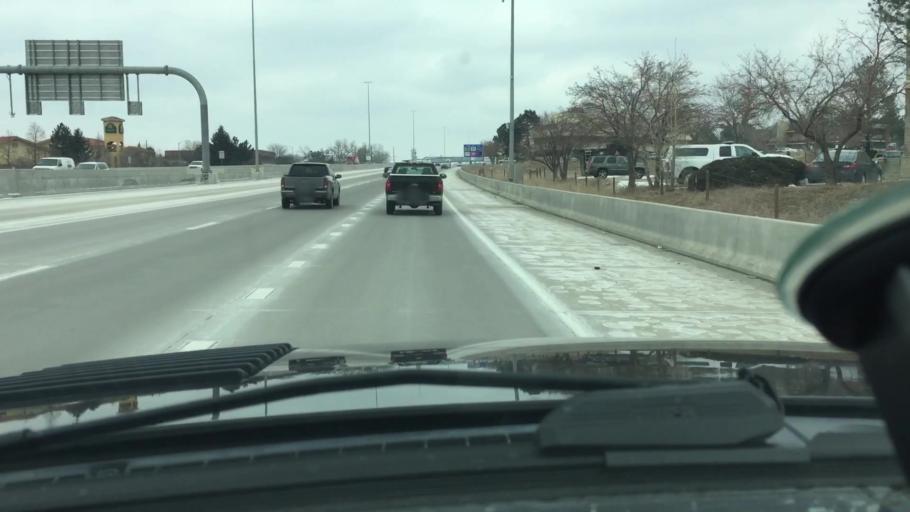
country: US
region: Colorado
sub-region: Adams County
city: Westminster
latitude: 39.8520
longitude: -105.0493
